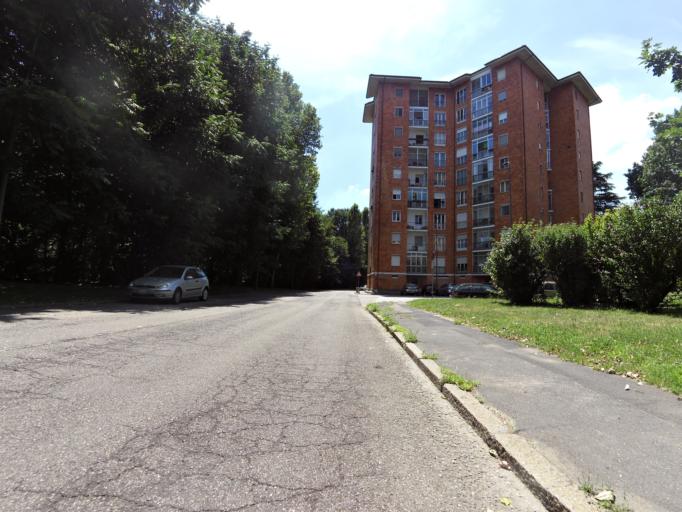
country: IT
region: Lombardy
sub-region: Citta metropolitana di Milano
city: Novegro-Tregarezzo-San Felice
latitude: 45.4896
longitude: 9.2481
